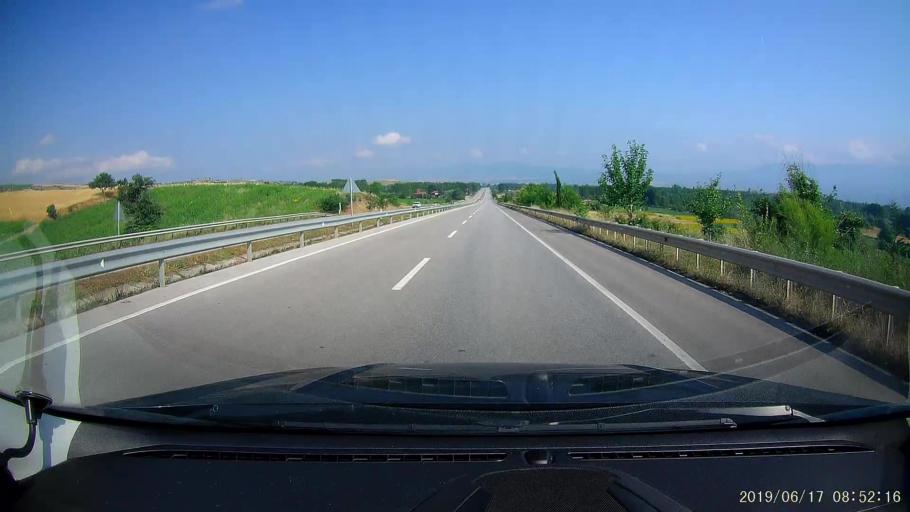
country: TR
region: Tokat
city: Erbaa
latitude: 40.6952
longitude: 36.4997
